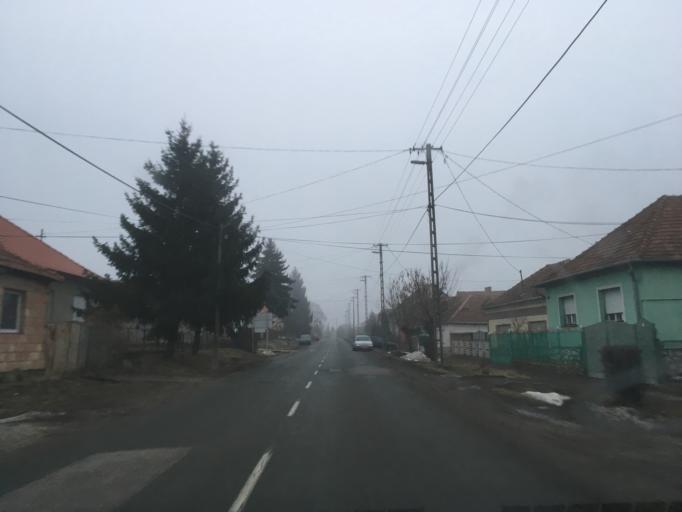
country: HU
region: Heves
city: Kerecsend
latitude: 47.7950
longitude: 20.3481
